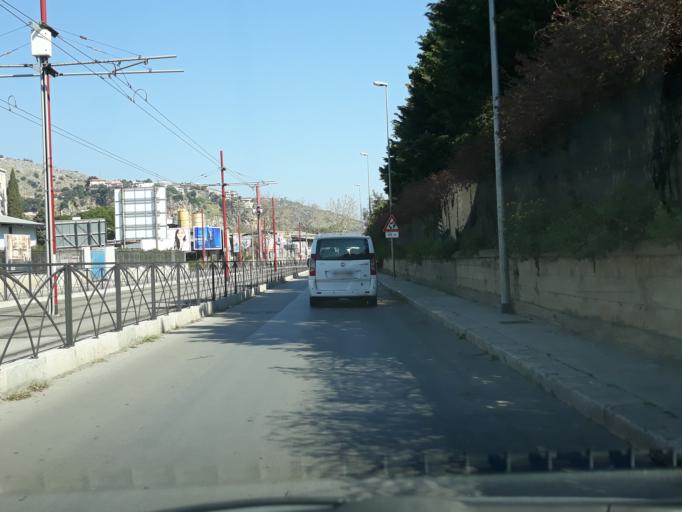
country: IT
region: Sicily
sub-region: Palermo
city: Palermo
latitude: 38.1292
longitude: 13.3030
